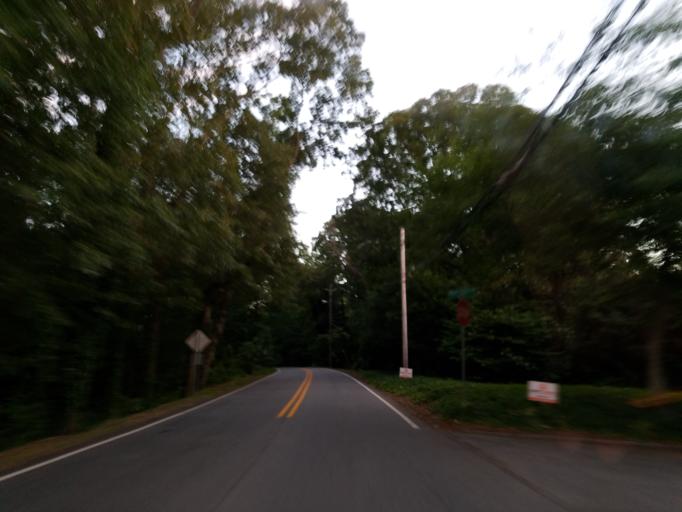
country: US
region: Georgia
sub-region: Fulton County
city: Sandy Springs
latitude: 33.8850
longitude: -84.4062
